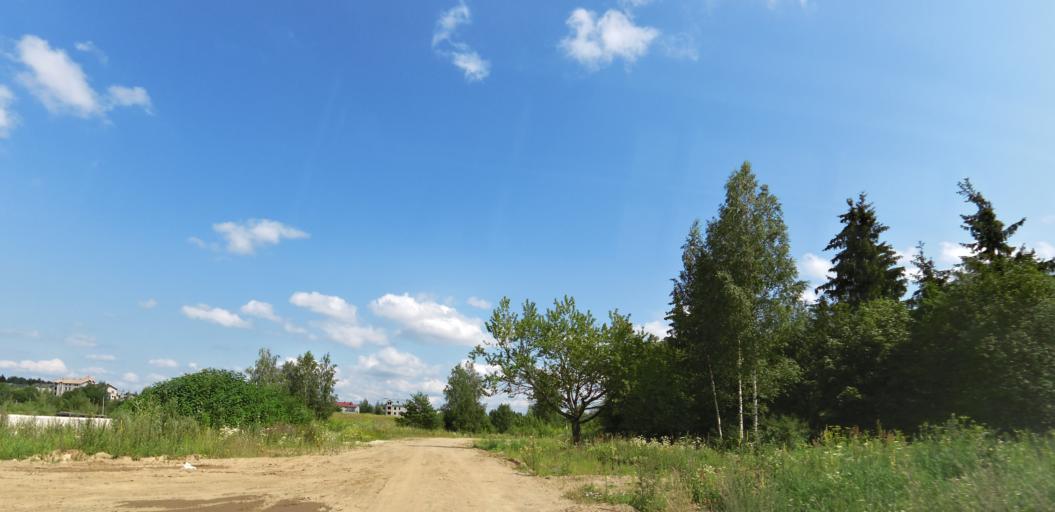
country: LT
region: Vilnius County
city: Pilaite
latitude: 54.7165
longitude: 25.1622
